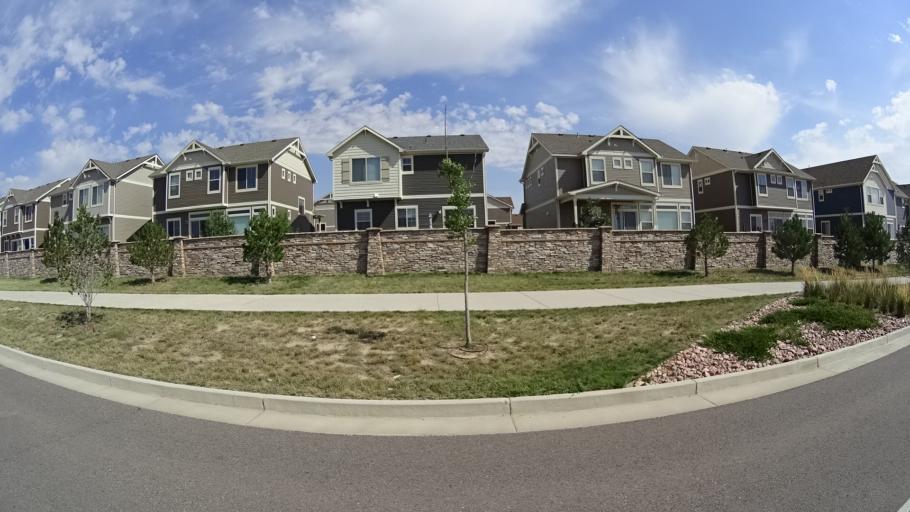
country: US
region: Colorado
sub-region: El Paso County
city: Cimarron Hills
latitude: 38.9267
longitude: -104.6706
